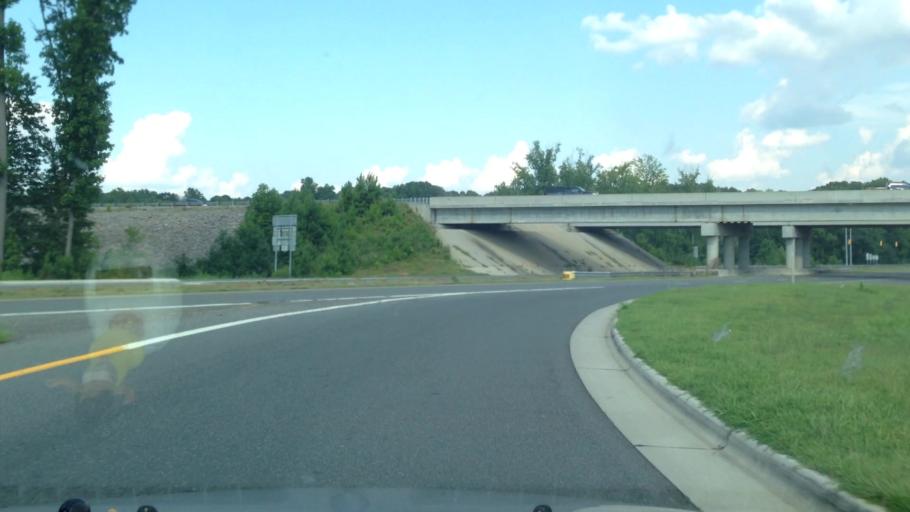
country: US
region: North Carolina
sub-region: Lee County
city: Sanford
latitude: 35.4469
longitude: -79.1206
